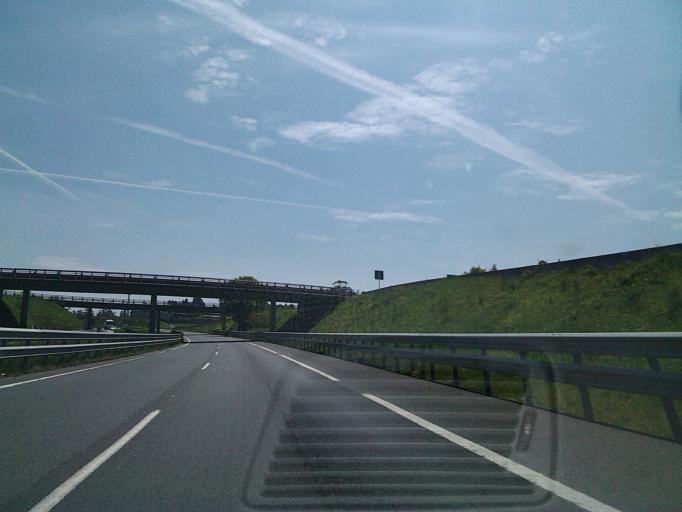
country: ES
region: Galicia
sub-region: Provincia da Coruna
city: Santiago de Compostela
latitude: 42.8975
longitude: -8.4851
